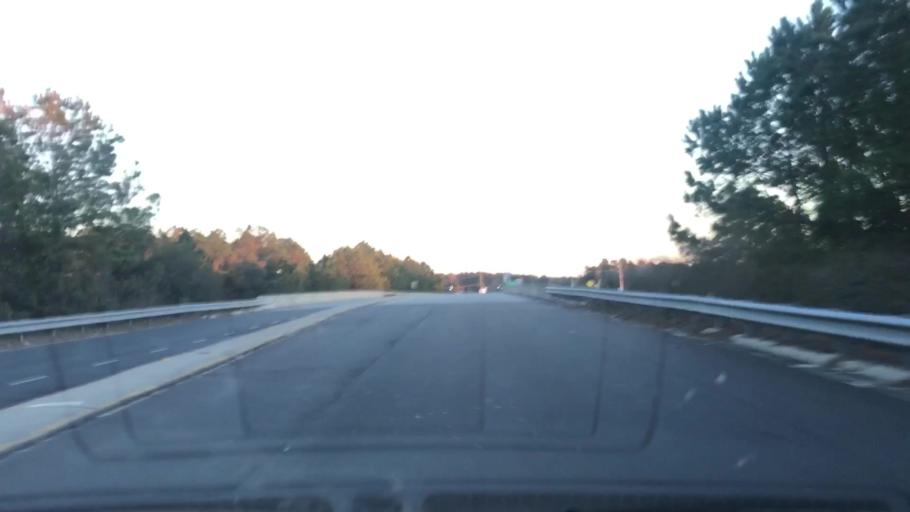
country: US
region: North Carolina
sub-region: Brunswick County
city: Shallotte
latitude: 33.9766
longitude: -78.4056
